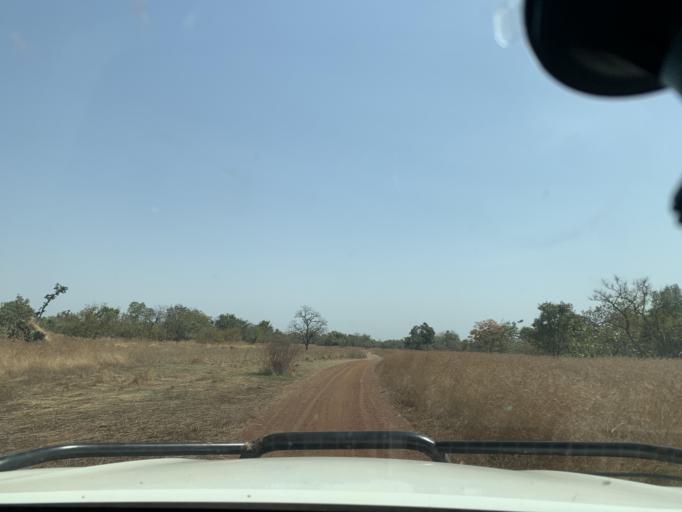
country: ML
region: Sikasso
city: Kolondieba
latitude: 10.8339
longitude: -6.7858
